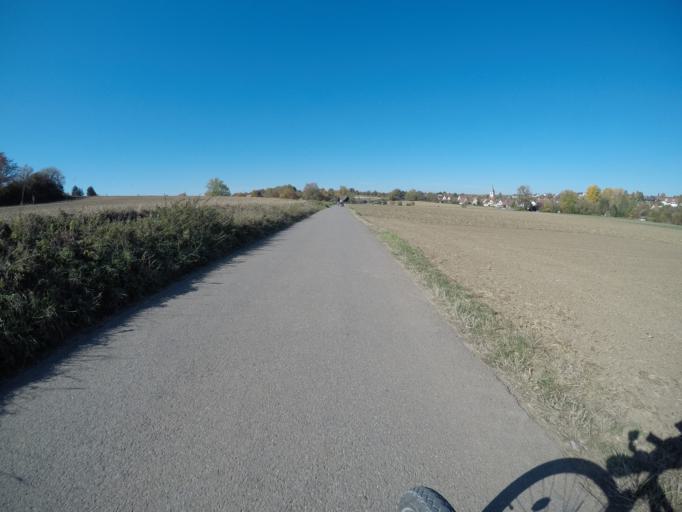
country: DE
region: Baden-Wuerttemberg
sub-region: Tuebingen Region
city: Rottenburg
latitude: 48.5304
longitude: 8.9517
